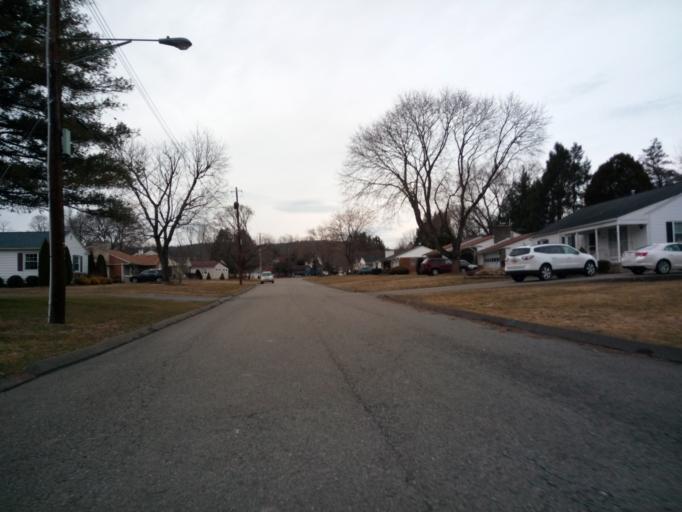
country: US
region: New York
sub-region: Chemung County
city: West Elmira
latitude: 42.0764
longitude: -76.8544
